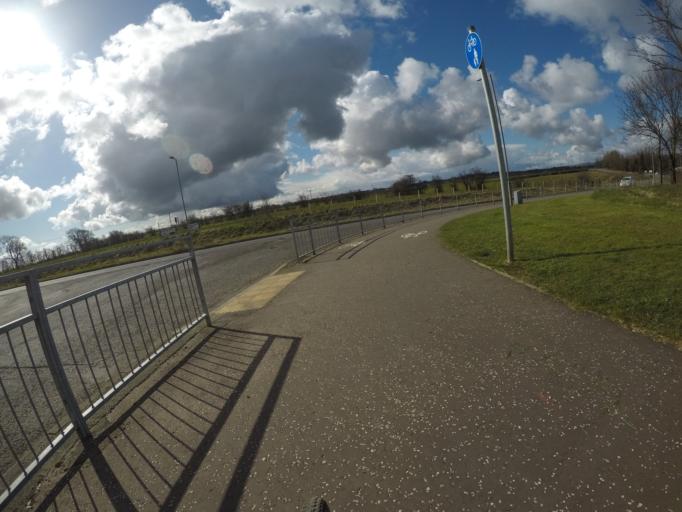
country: GB
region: Scotland
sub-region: North Ayrshire
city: Beith
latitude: 55.7437
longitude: -4.6463
